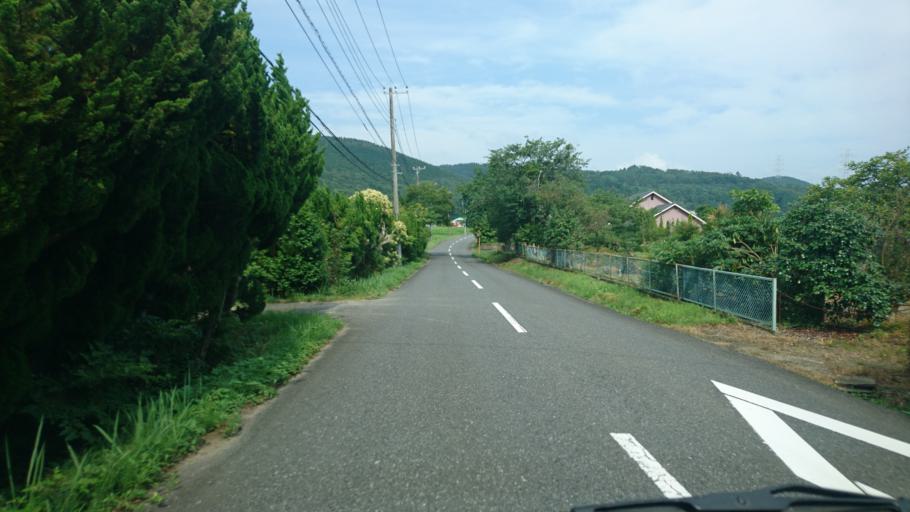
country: JP
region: Chiba
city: Kimitsu
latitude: 35.2930
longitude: 139.9875
